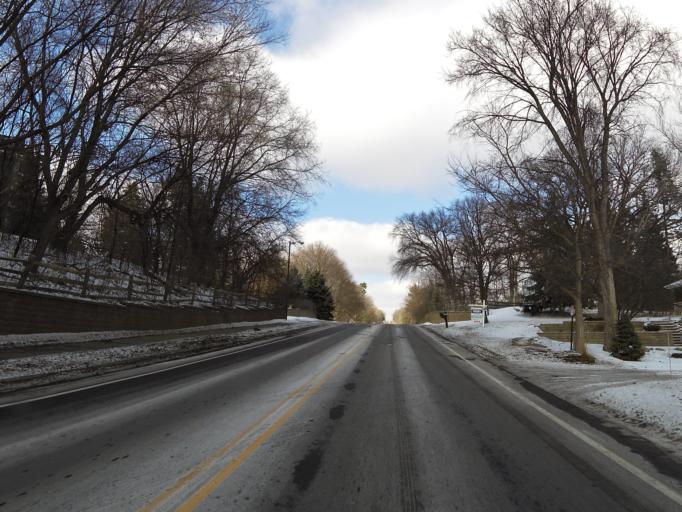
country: US
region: Minnesota
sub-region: Hennepin County
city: Hopkins
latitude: 44.9124
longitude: -93.4678
